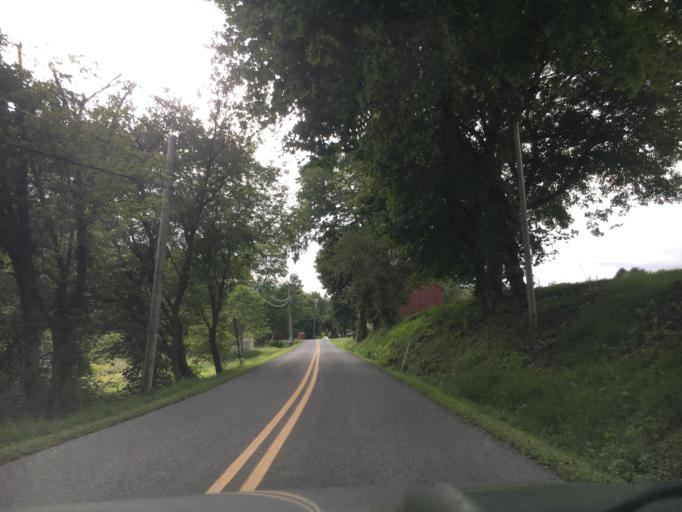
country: US
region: Pennsylvania
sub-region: Lehigh County
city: Schnecksville
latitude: 40.6192
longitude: -75.7104
